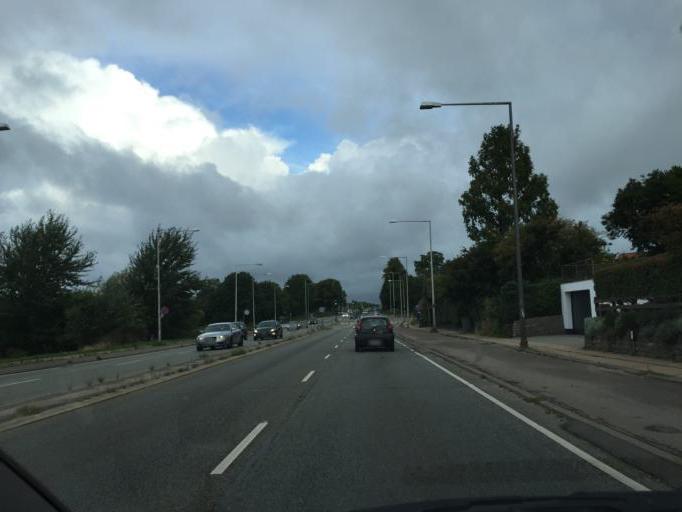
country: DK
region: Capital Region
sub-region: Kobenhavn
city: Vanlose
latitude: 55.7116
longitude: 12.5060
